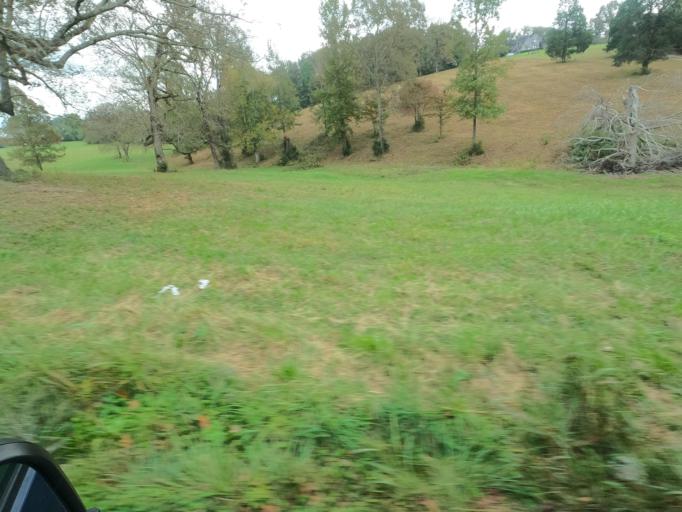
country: US
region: Tennessee
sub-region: Cheatham County
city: Kingston Springs
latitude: 36.0985
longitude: -87.0885
